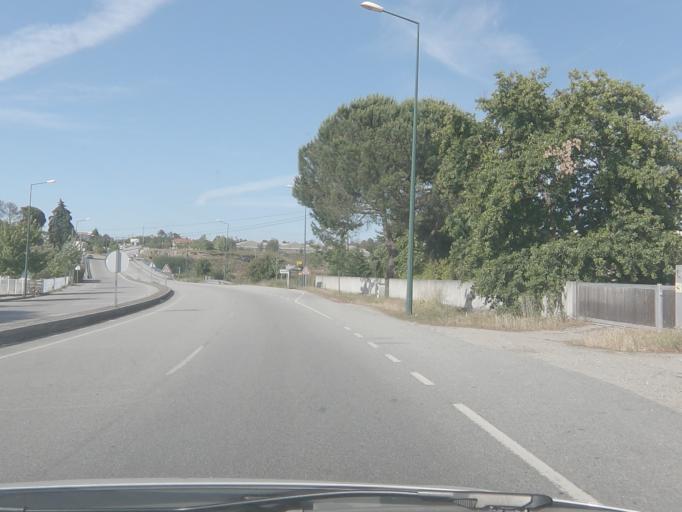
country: PT
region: Viseu
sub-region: Viseu
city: Viseu
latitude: 40.6224
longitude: -7.9448
